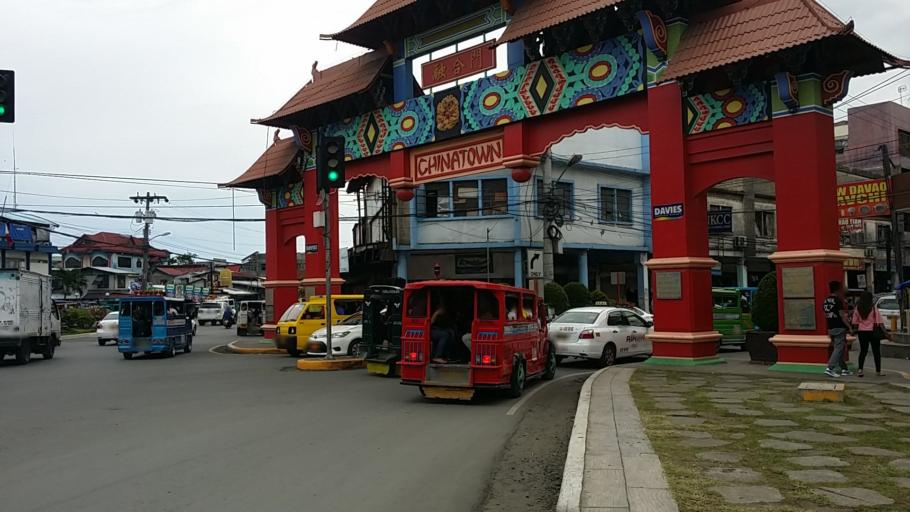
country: PH
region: Davao
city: Davao
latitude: 7.0745
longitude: 125.6248
